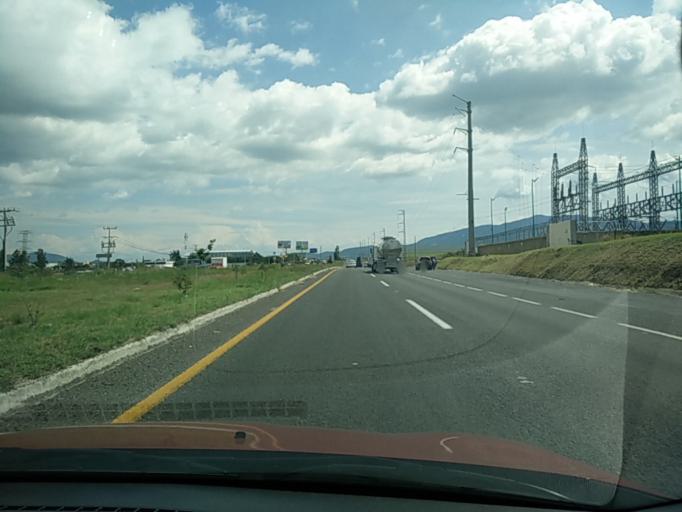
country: MX
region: Jalisco
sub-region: Ixtlahuacan de los Membrillos
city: Los Olivos
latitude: 20.4415
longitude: -103.2449
